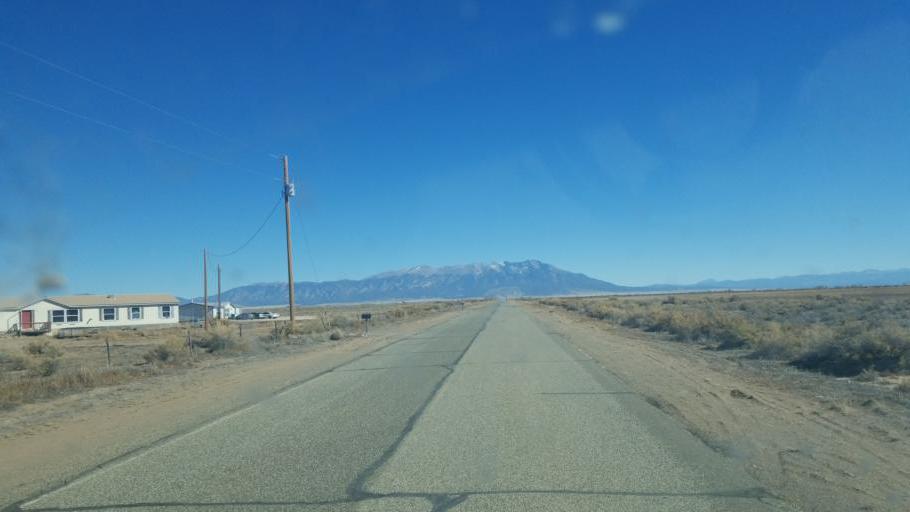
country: US
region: Colorado
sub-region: Alamosa County
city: Alamosa
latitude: 37.5746
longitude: -105.9011
